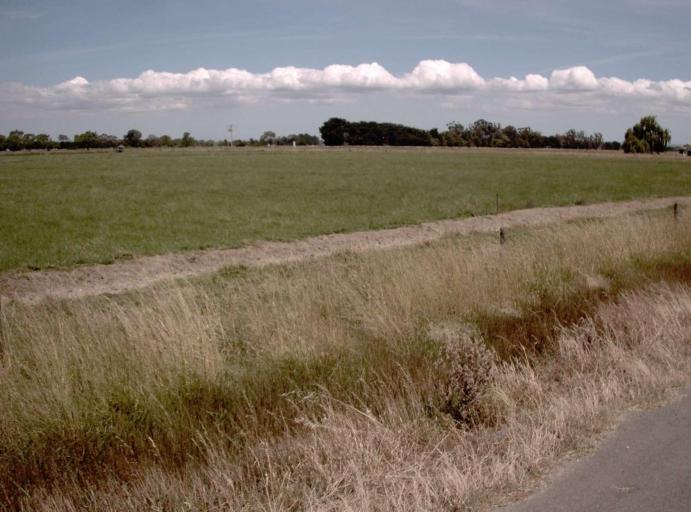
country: AU
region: Victoria
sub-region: Wellington
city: Heyfield
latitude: -38.0244
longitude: 146.8806
